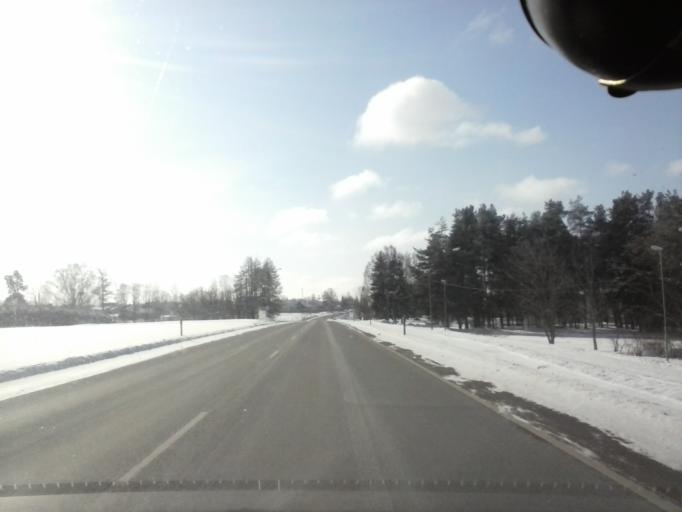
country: EE
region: Viljandimaa
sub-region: Viiratsi vald
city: Viiratsi
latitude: 58.3695
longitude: 25.6475
